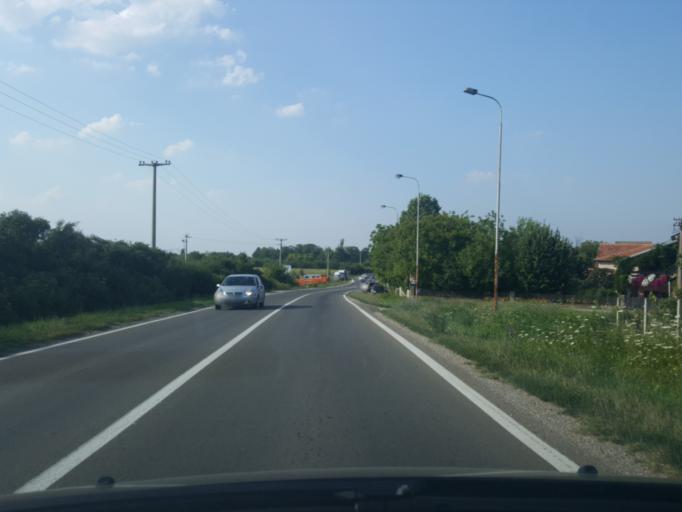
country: RS
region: Central Serbia
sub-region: Belgrade
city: Mladenovac
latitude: 44.4213
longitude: 20.6816
